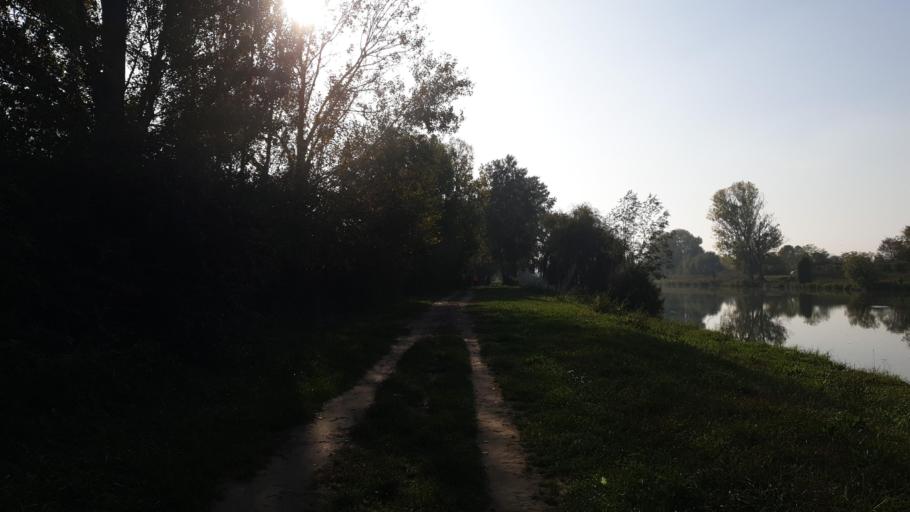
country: IT
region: Veneto
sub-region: Provincia di Venezia
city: Vigonovo
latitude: 45.3902
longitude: 11.9962
